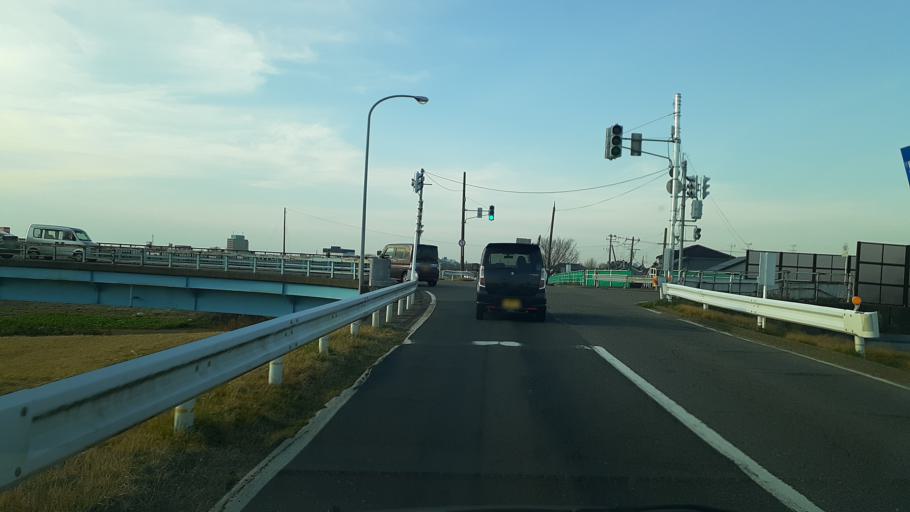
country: JP
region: Niigata
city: Niigata-shi
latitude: 37.8542
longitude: 139.0250
